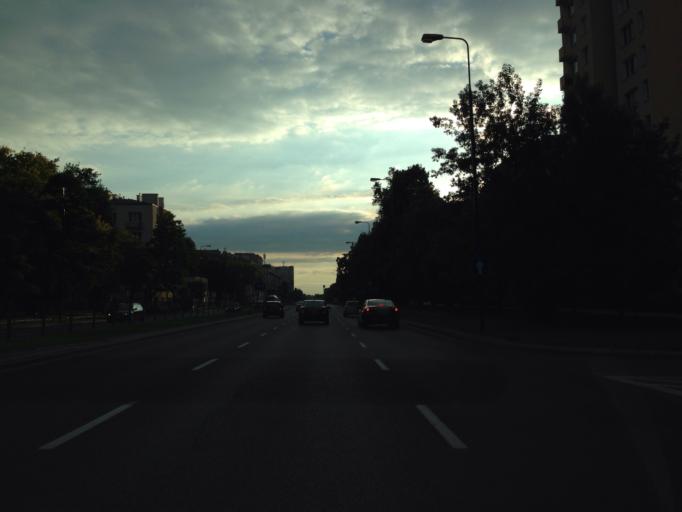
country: PL
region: Masovian Voivodeship
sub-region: Warszawa
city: Wola
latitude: 52.2369
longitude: 20.9688
